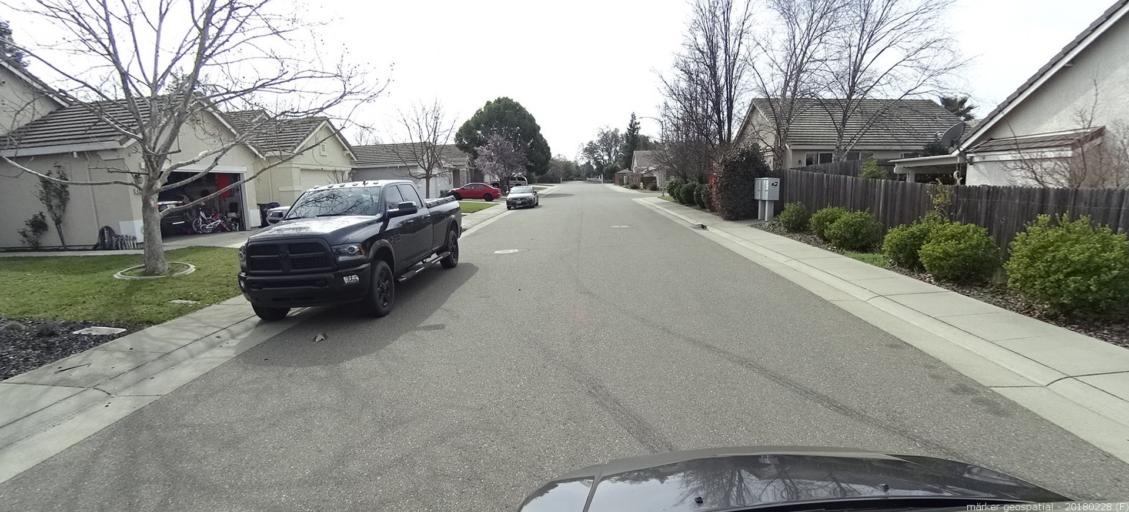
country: US
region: California
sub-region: Sacramento County
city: Antelope
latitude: 38.7212
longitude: -121.3283
